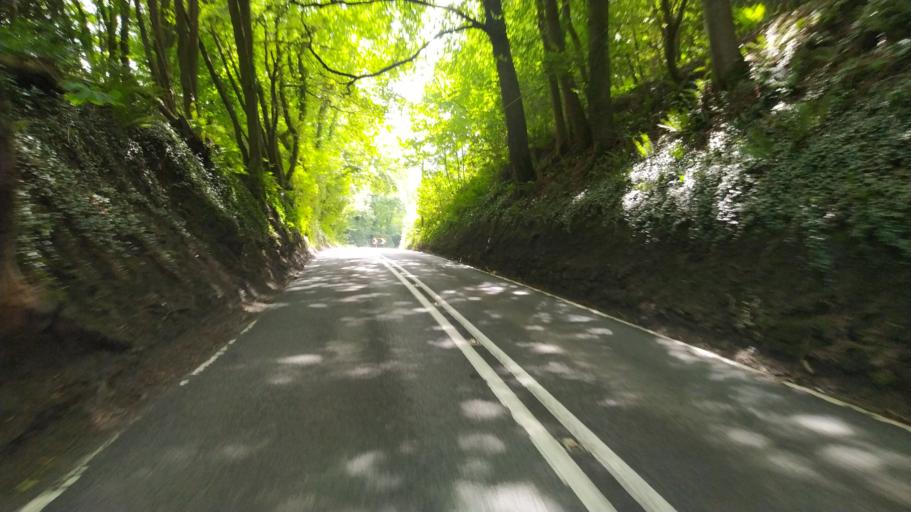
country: GB
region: England
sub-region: Dorset
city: Shaftesbury
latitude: 51.0305
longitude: -2.1890
